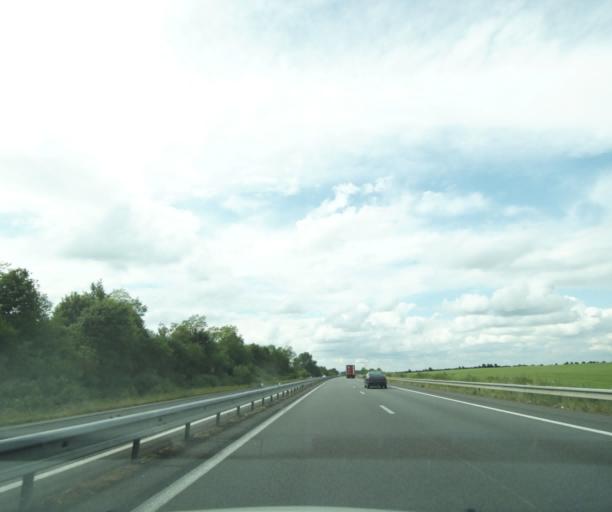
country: FR
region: Centre
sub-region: Departement du Cher
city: Mehun-sur-Yevre
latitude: 47.1182
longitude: 2.1956
